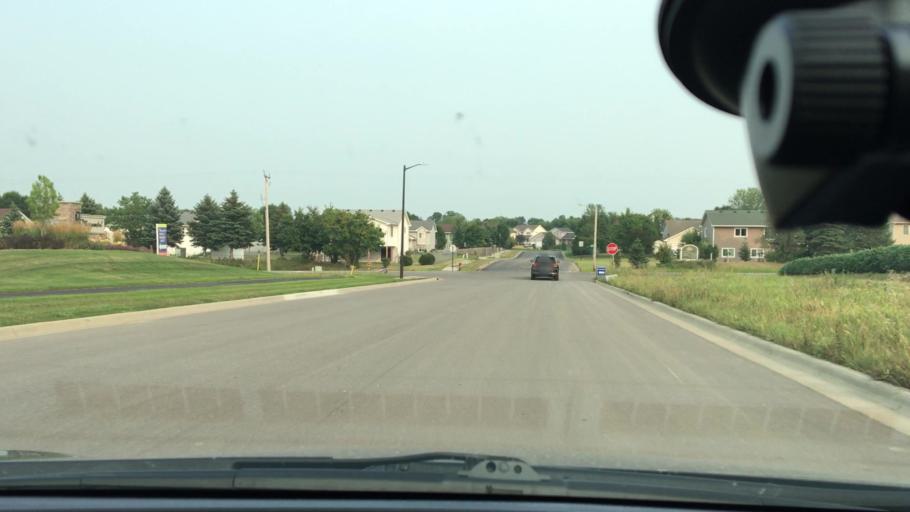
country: US
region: Minnesota
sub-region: Wright County
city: Saint Michael
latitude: 45.2027
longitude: -93.6822
